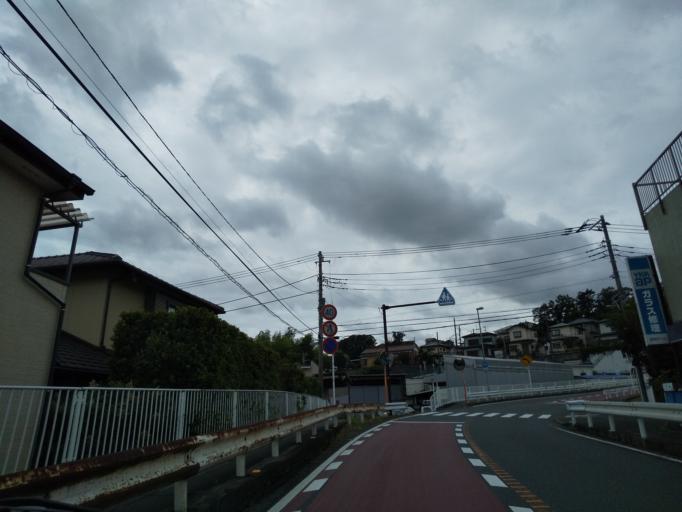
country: JP
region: Kanagawa
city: Zama
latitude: 35.5144
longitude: 139.3646
